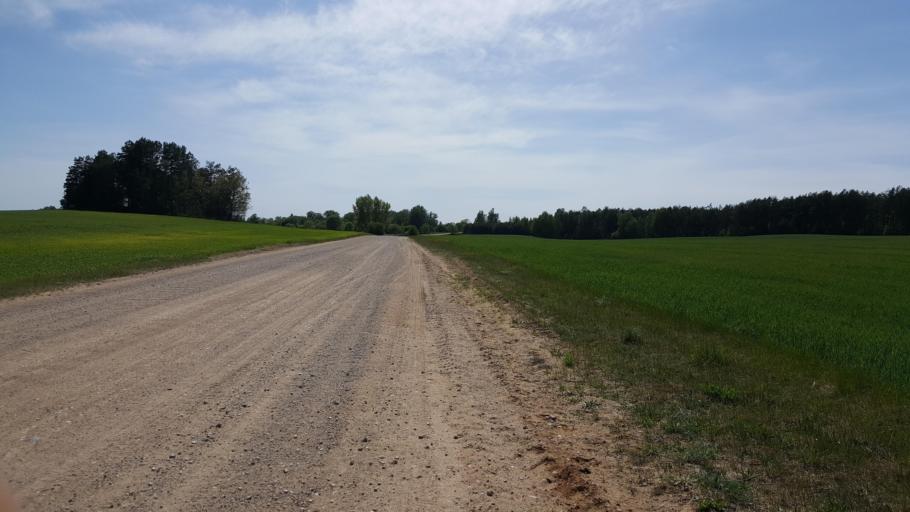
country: BY
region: Brest
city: Zhabinka
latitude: 52.3423
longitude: 24.1081
